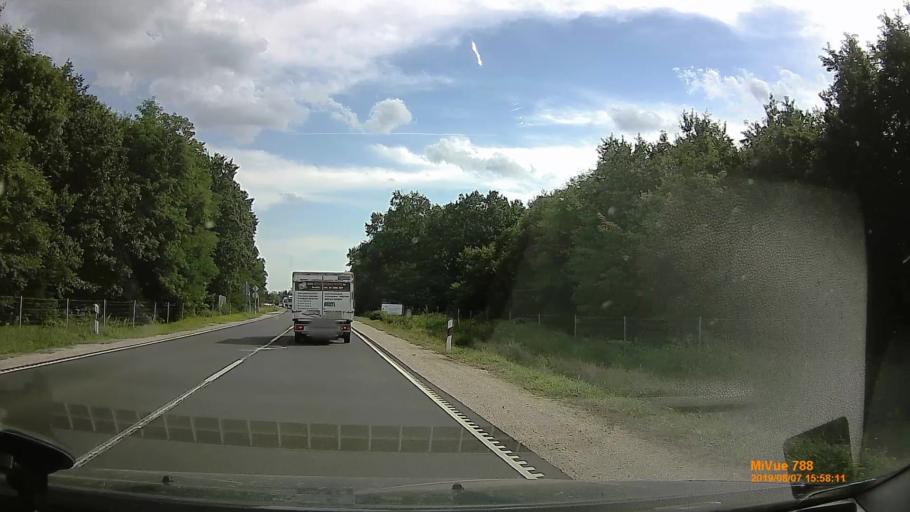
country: HU
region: Vas
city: Kormend
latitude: 47.0303
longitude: 16.6124
